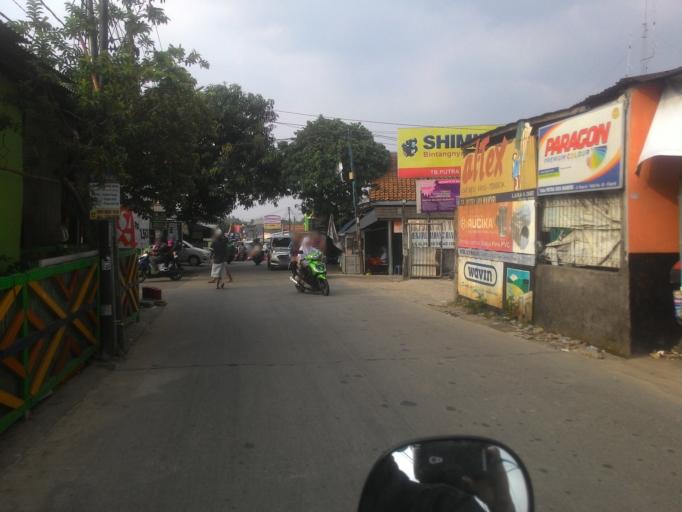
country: ID
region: West Java
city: Cibinong
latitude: -6.4616
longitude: 106.8402
